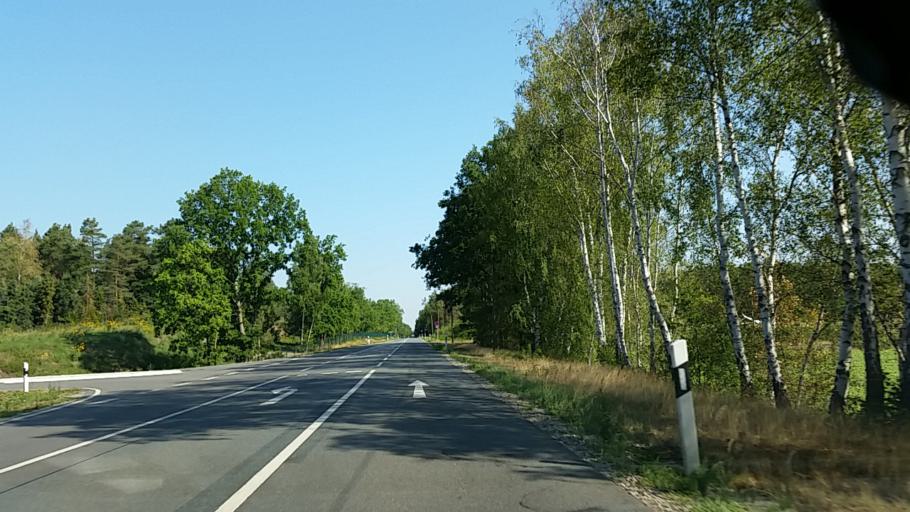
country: DE
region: Lower Saxony
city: Sassenburg
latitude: 52.5637
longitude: 10.6767
